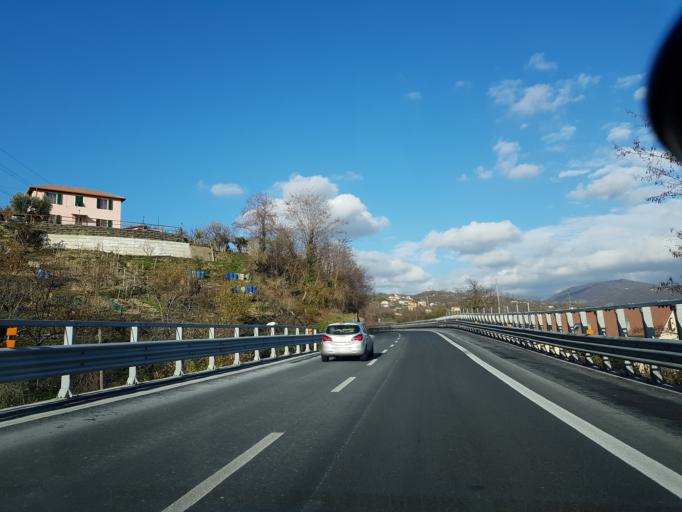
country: IT
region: Liguria
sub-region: Provincia di Genova
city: Pedemonte
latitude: 44.4977
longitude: 8.9165
